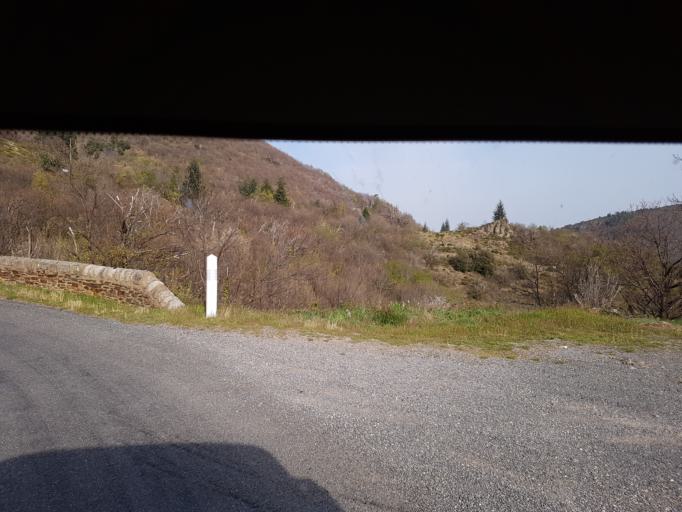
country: FR
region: Languedoc-Roussillon
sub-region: Departement du Gard
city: Branoux-les-Taillades
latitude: 44.3333
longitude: 3.8781
